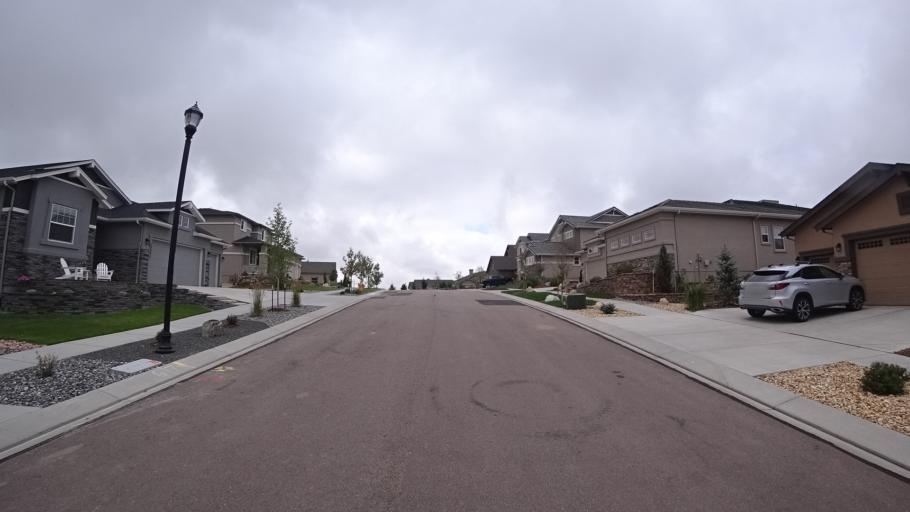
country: US
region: Colorado
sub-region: El Paso County
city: Gleneagle
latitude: 39.0128
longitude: -104.7917
